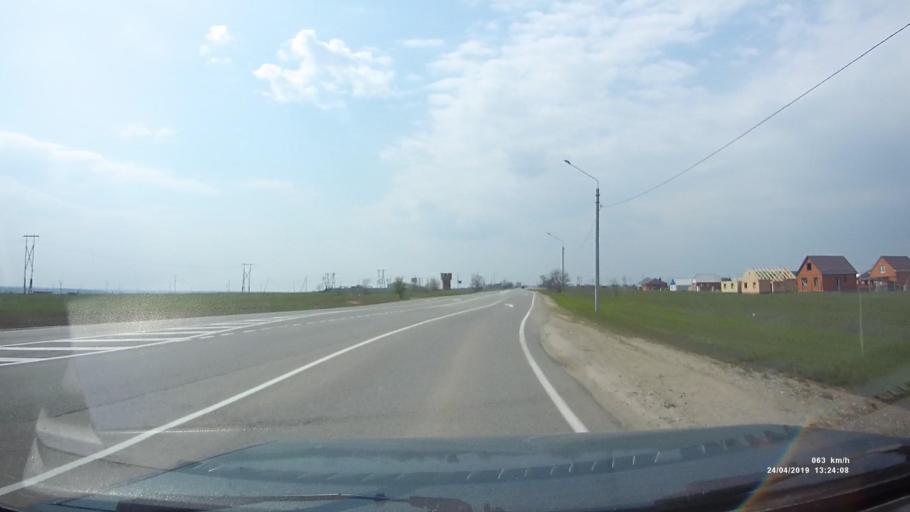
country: RU
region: Kalmykiya
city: Elista
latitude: 46.2835
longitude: 44.2596
